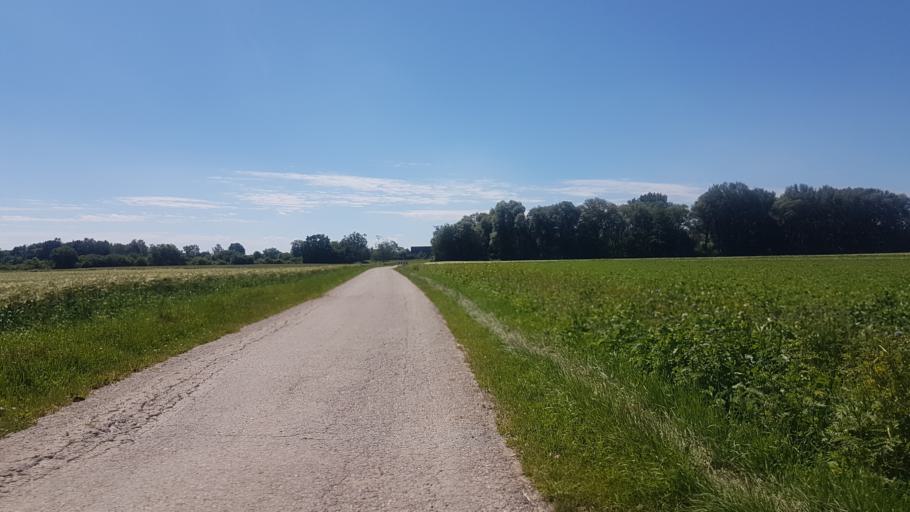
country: DE
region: Bavaria
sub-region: Upper Bavaria
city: Weichering
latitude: 48.7232
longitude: 11.3128
